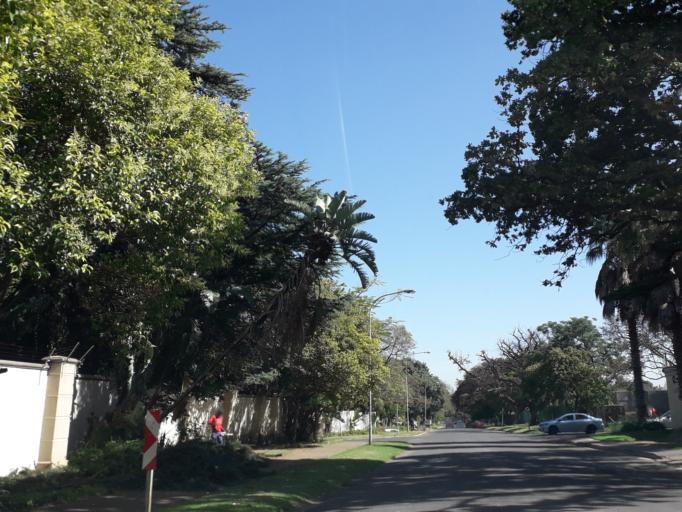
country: ZA
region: Gauteng
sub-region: City of Johannesburg Metropolitan Municipality
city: Johannesburg
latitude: -26.1589
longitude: 28.0618
